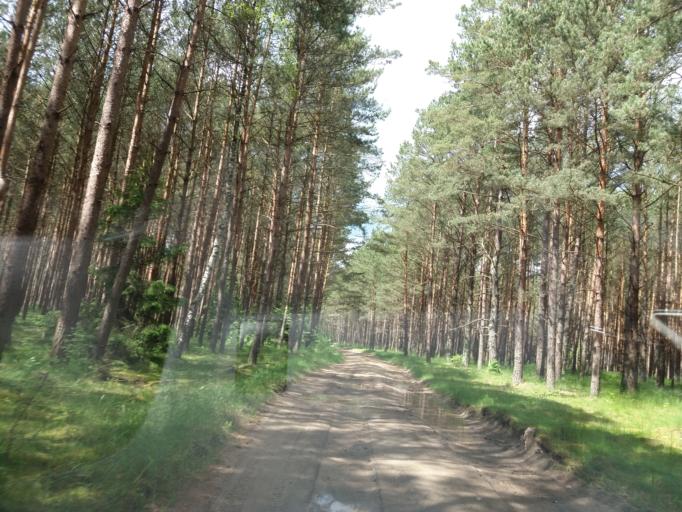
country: PL
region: West Pomeranian Voivodeship
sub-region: Powiat choszczenski
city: Drawno
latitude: 53.2829
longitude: 15.7258
